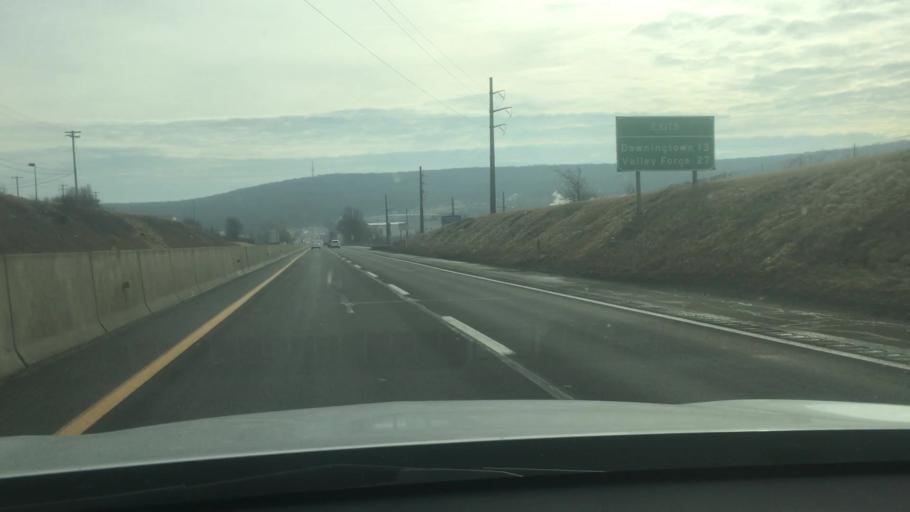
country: US
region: Pennsylvania
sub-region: Chester County
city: Elverson
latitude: 40.1540
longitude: -75.8678
